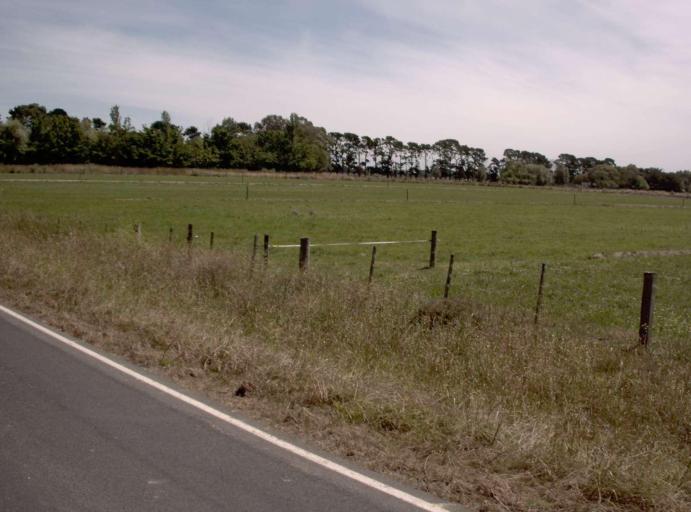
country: AU
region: Victoria
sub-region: Wellington
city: Heyfield
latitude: -38.0704
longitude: 146.8708
